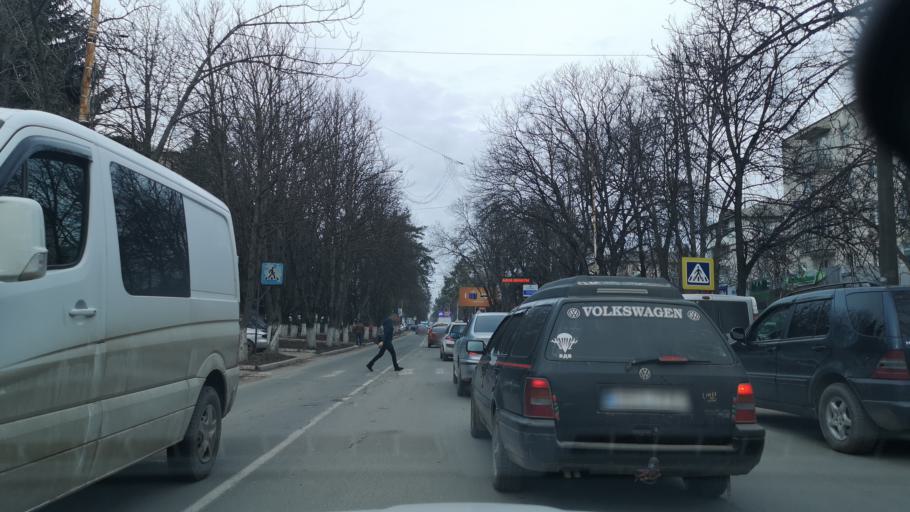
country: MD
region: Raionul Edinet
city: Edinet
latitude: 48.1680
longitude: 27.3081
